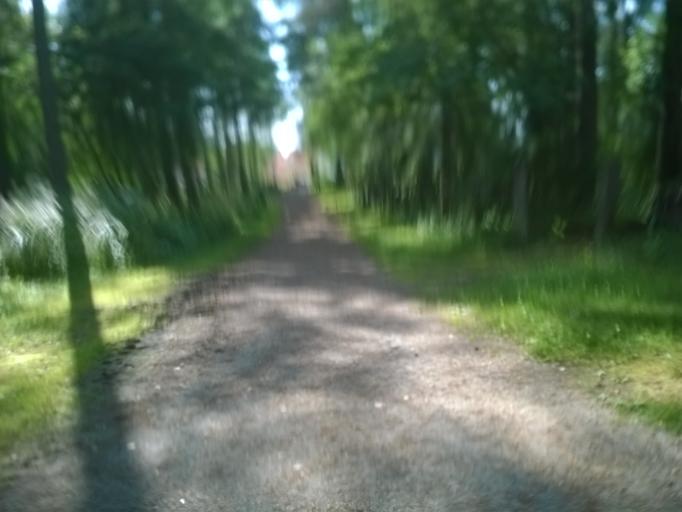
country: FI
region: Kainuu
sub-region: Kehys-Kainuu
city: Kuhmo
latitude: 64.1317
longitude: 29.5241
